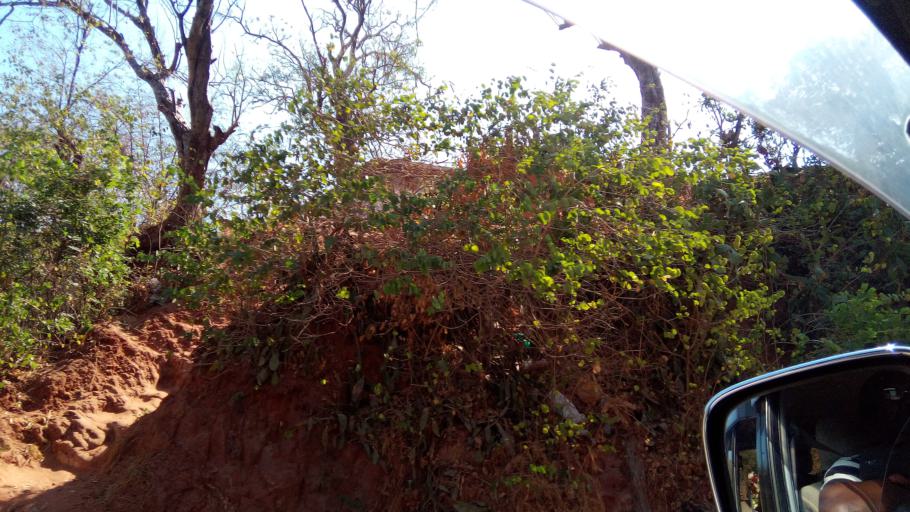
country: CD
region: Katanga
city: Kalemie
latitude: -5.9373
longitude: 29.1861
